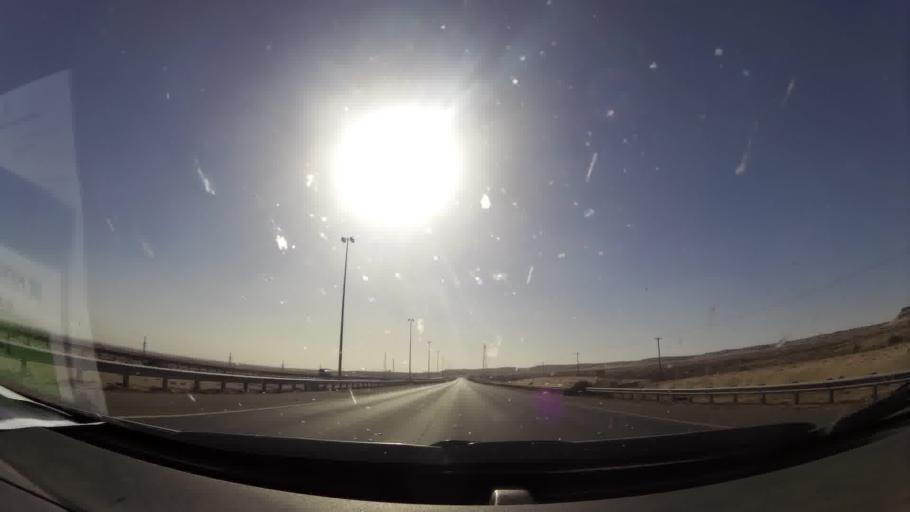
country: KW
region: Muhafazat al Jahra'
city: Al Jahra'
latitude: 29.4874
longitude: 47.7804
